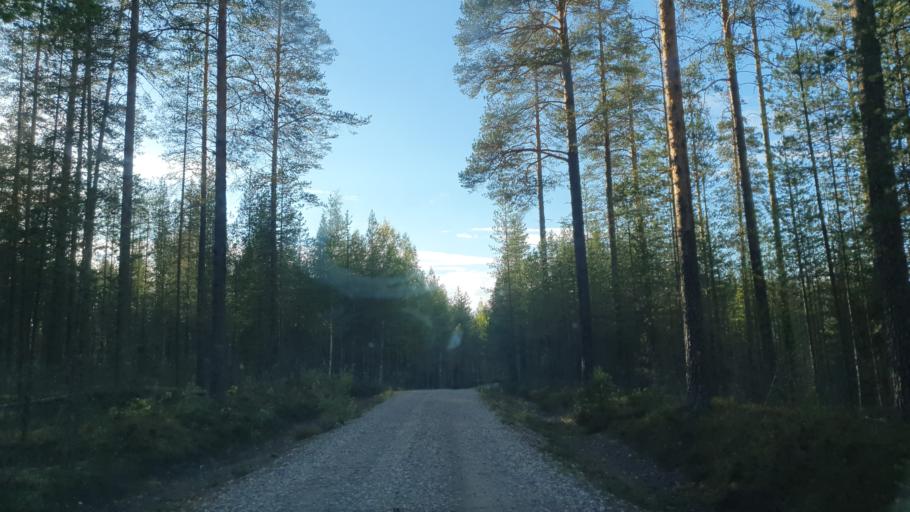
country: FI
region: Kainuu
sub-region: Kehys-Kainuu
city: Kuhmo
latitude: 64.3272
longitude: 30.0374
